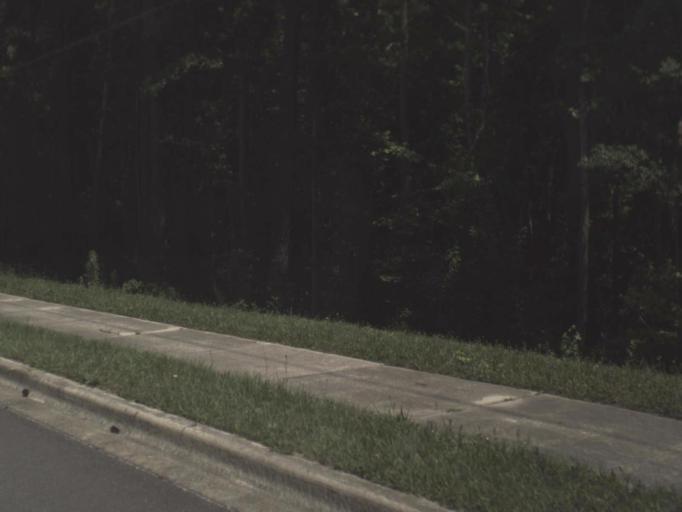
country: US
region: Florida
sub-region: Baker County
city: Macclenny
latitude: 30.2786
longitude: -82.1479
